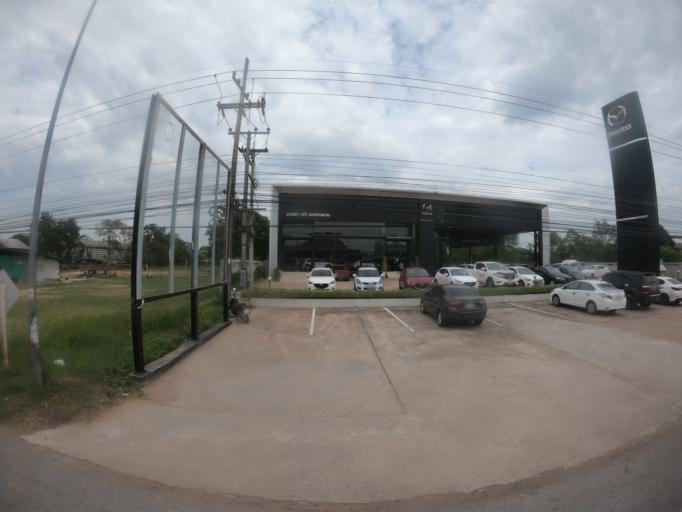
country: TH
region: Maha Sarakham
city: Maha Sarakham
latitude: 16.1655
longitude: 103.3334
